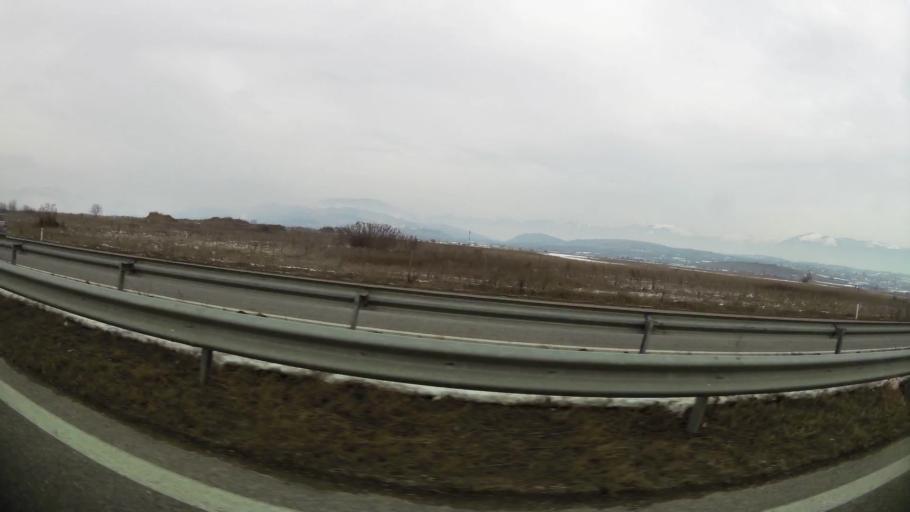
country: MK
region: Suto Orizari
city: Suto Orizare
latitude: 42.0530
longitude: 21.3953
